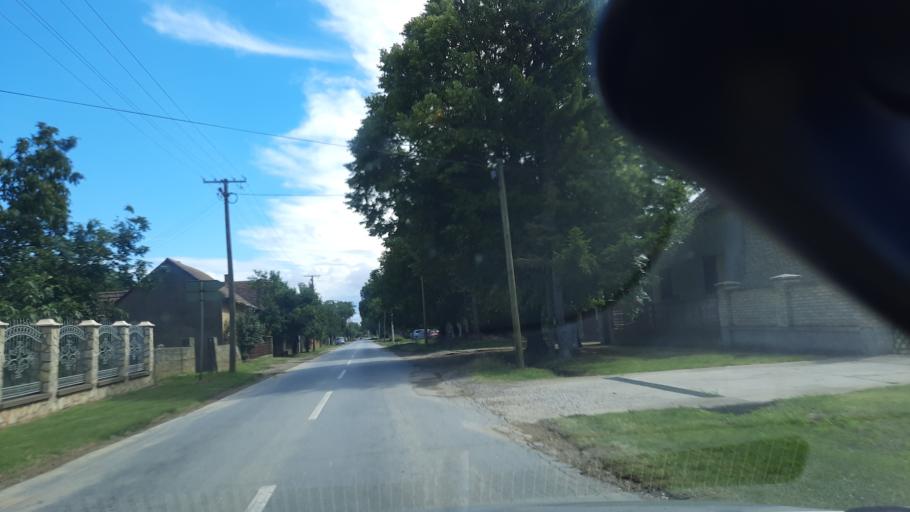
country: RS
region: Autonomna Pokrajina Vojvodina
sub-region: Sremski Okrug
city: Sremska Mitrovica
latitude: 45.1166
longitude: 19.5664
